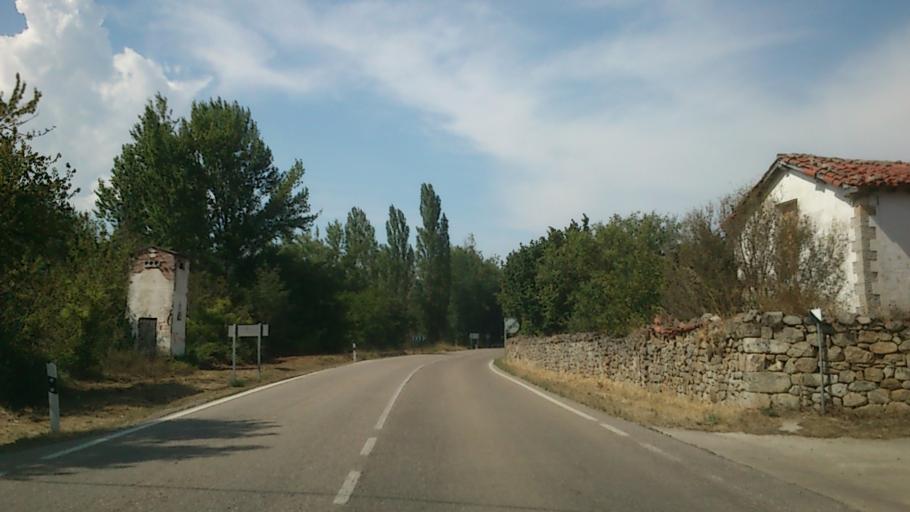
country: ES
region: Castille and Leon
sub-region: Provincia de Burgos
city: Medina de Pomar
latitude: 43.0148
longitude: -3.4833
